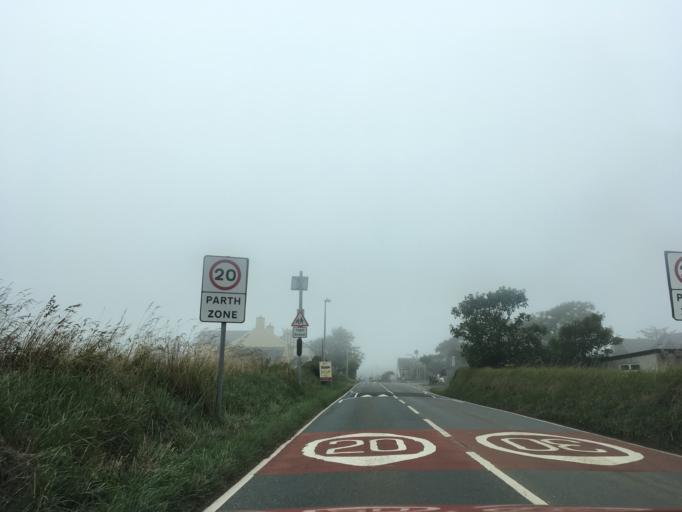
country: GB
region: Wales
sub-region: Pembrokeshire
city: Saint David's
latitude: 51.8811
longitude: -5.2546
